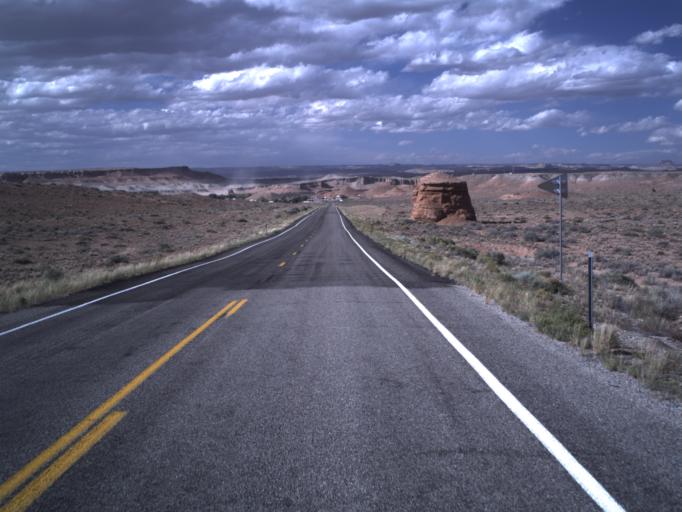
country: US
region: Utah
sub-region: Emery County
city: Ferron
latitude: 38.3546
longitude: -110.6965
